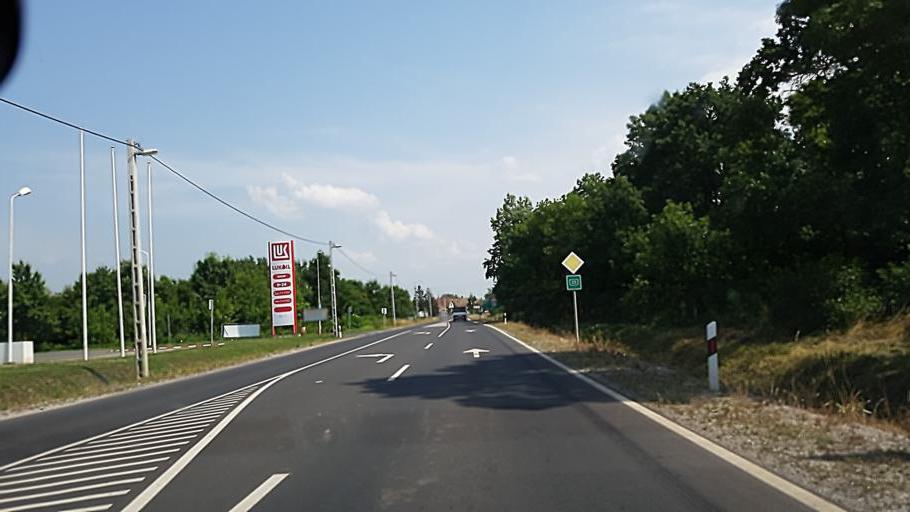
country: HU
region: Heves
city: Poroszlo
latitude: 47.6445
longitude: 20.6359
